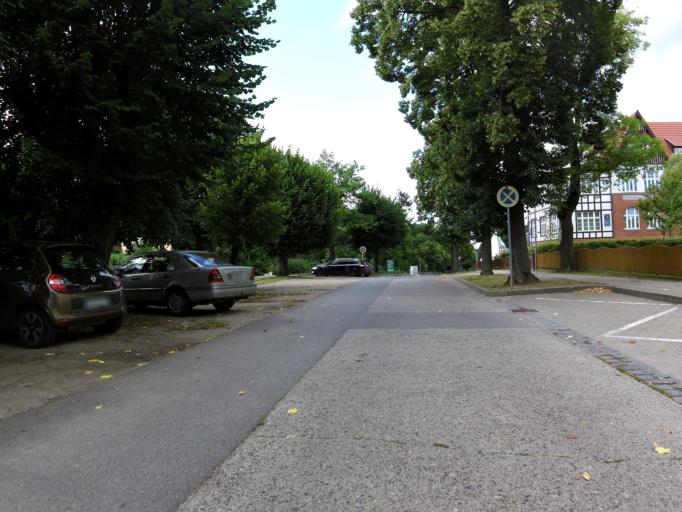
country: DE
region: Brandenburg
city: Lychen
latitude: 53.2042
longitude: 13.3214
